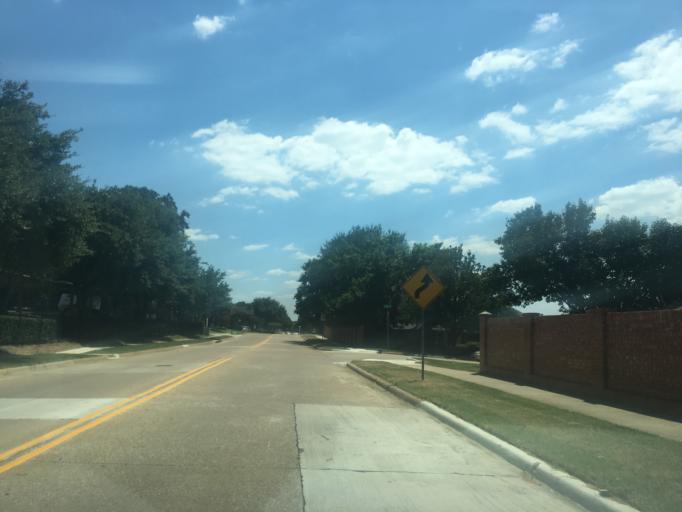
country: US
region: Texas
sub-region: Denton County
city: Lewisville
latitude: 33.0258
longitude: -96.9994
